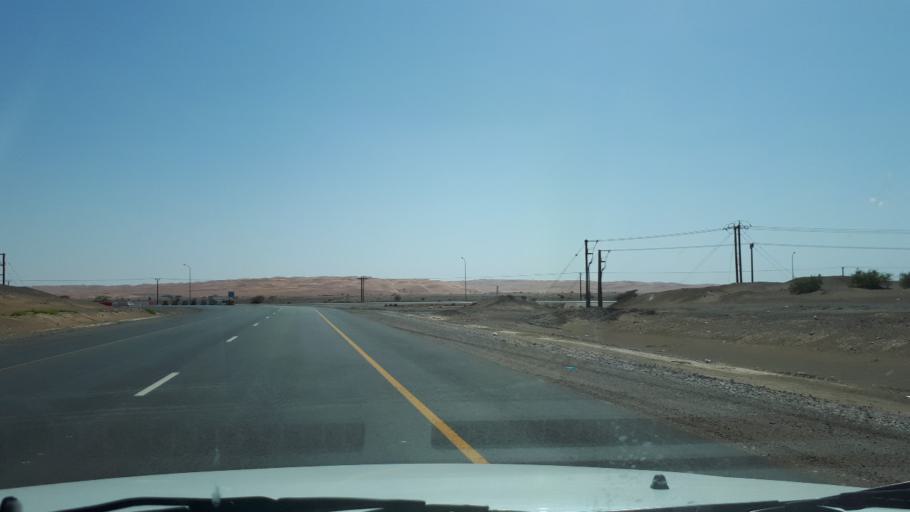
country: OM
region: Ash Sharqiyah
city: Al Qabil
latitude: 22.5214
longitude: 58.7387
